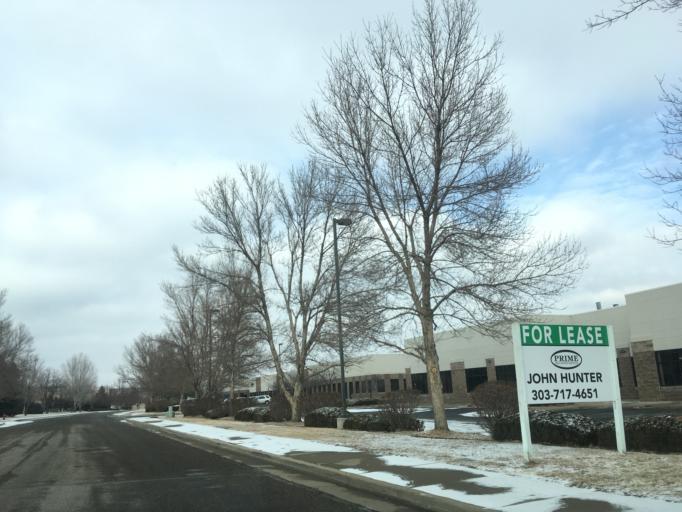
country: US
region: Colorado
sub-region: Boulder County
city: Lafayette
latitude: 39.9827
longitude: -105.0866
